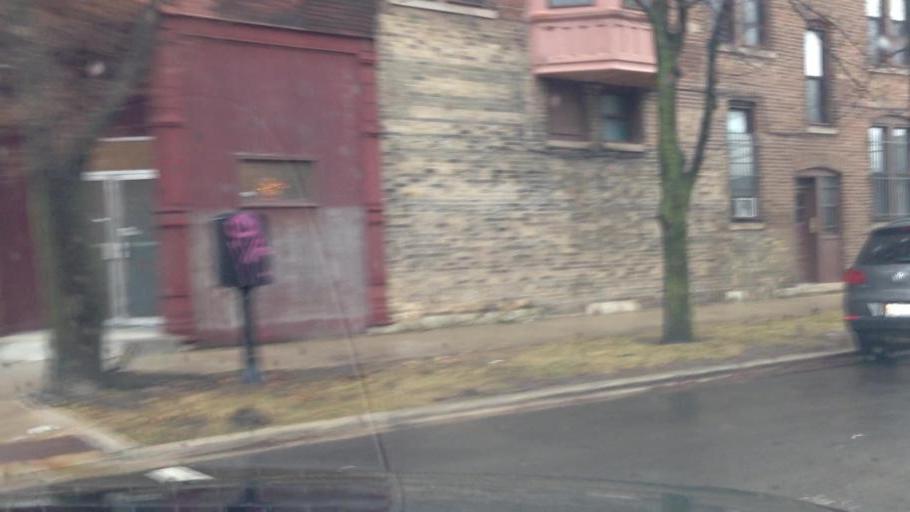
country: US
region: Illinois
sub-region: Cook County
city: Chicago
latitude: 41.8956
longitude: -87.6942
